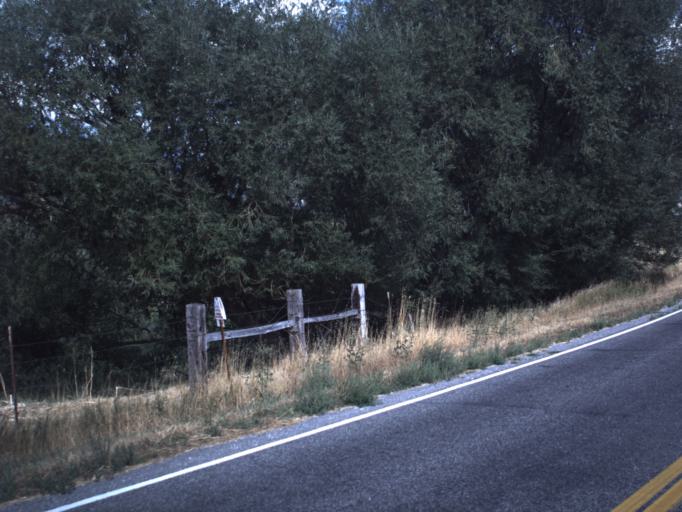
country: US
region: Utah
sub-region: Cache County
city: Lewiston
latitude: 41.9147
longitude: -111.9304
